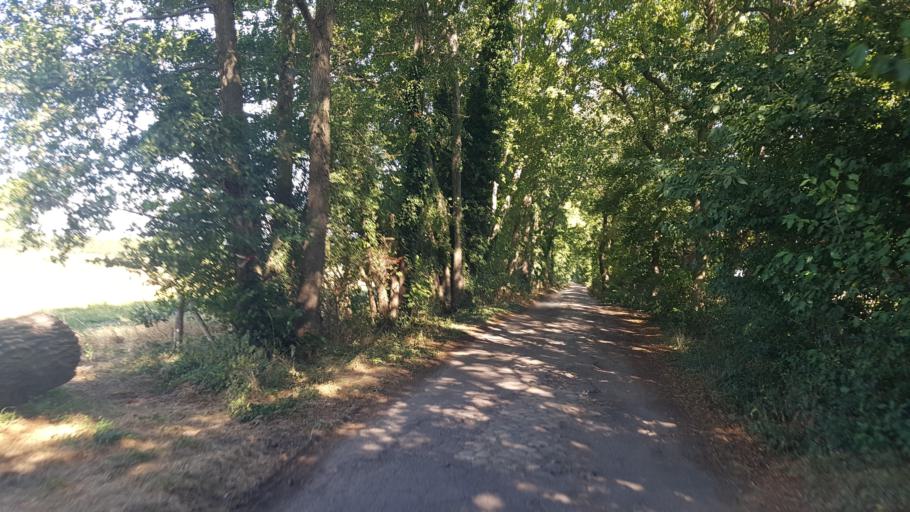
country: DE
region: Brandenburg
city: Brandenburg an der Havel
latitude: 52.3389
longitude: 12.5388
